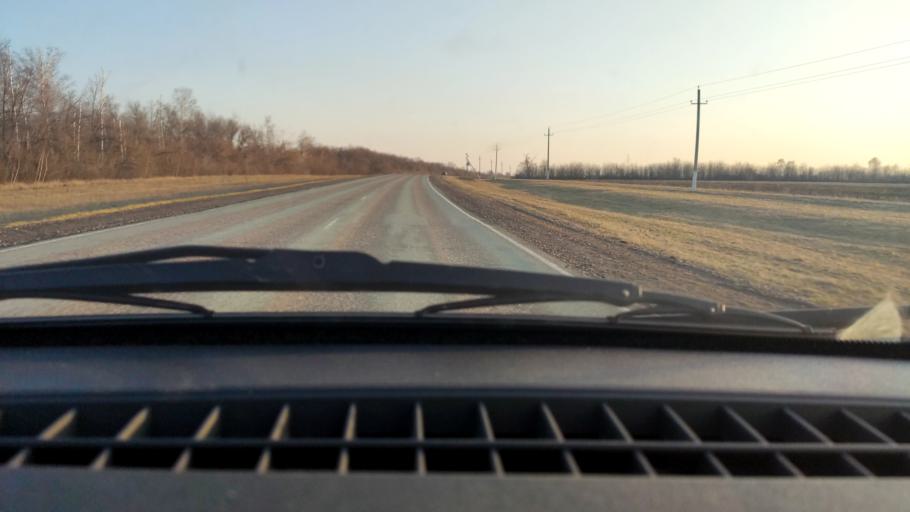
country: RU
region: Bashkortostan
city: Davlekanovo
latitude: 54.3308
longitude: 55.1663
